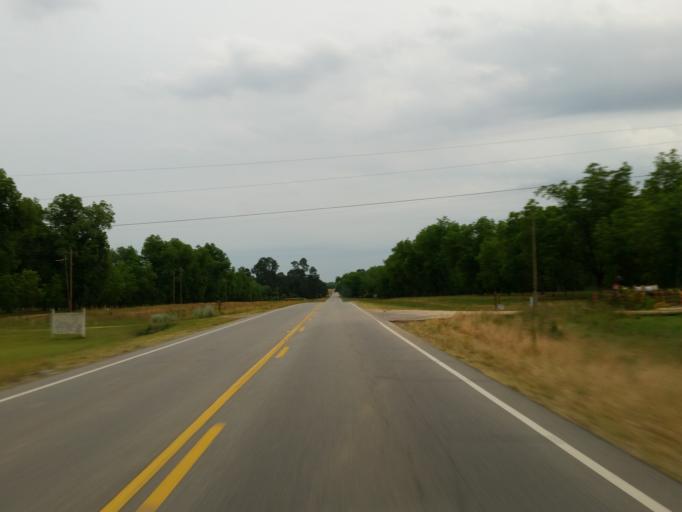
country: US
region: Georgia
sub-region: Dooly County
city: Vienna
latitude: 32.0466
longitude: -83.7962
